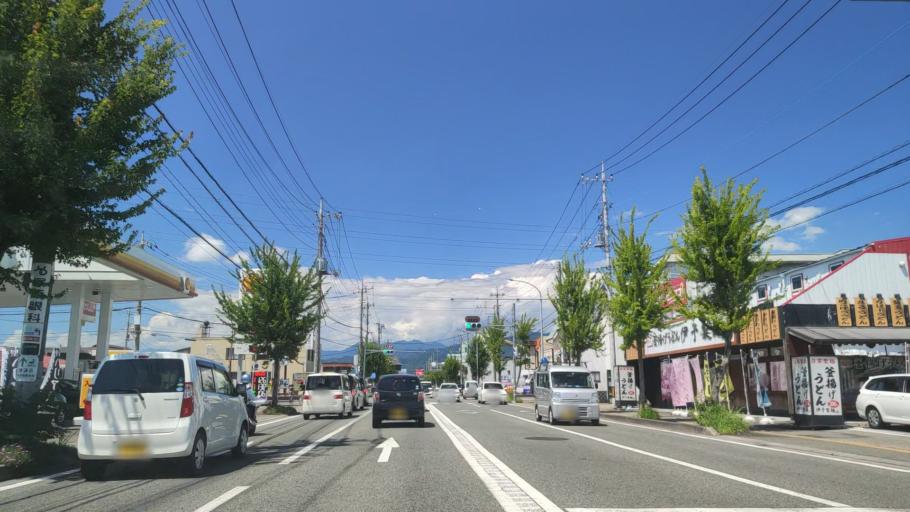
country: JP
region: Yamanashi
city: Kofu-shi
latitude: 35.6256
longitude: 138.5718
